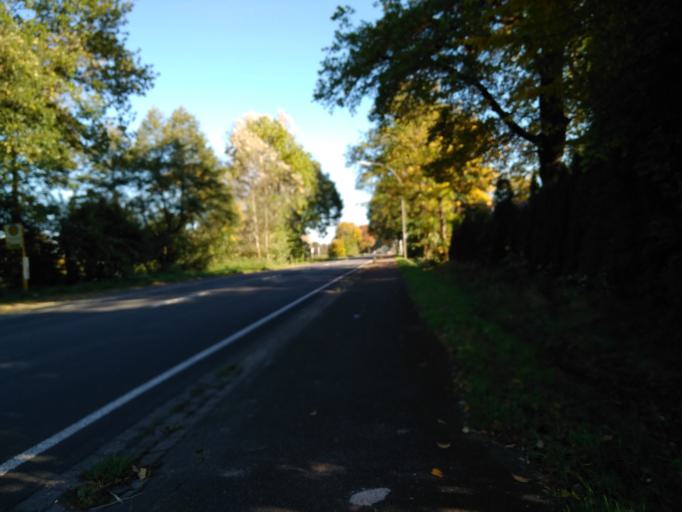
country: DE
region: North Rhine-Westphalia
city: Marl
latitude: 51.6395
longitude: 7.0697
